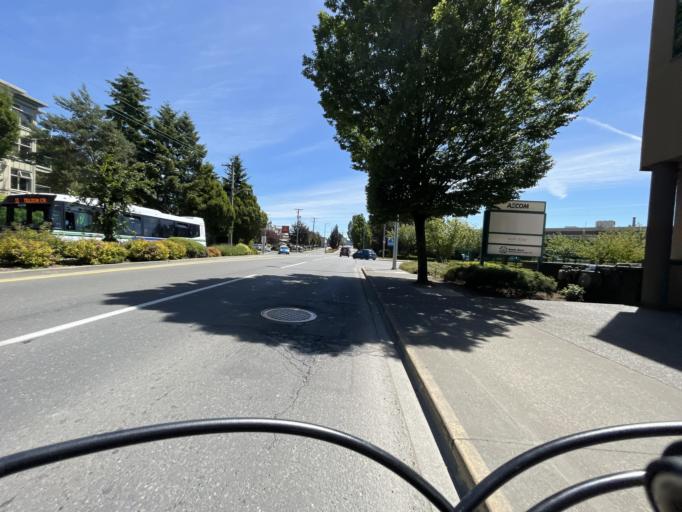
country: CA
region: British Columbia
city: Victoria
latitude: 48.4413
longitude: -123.3754
